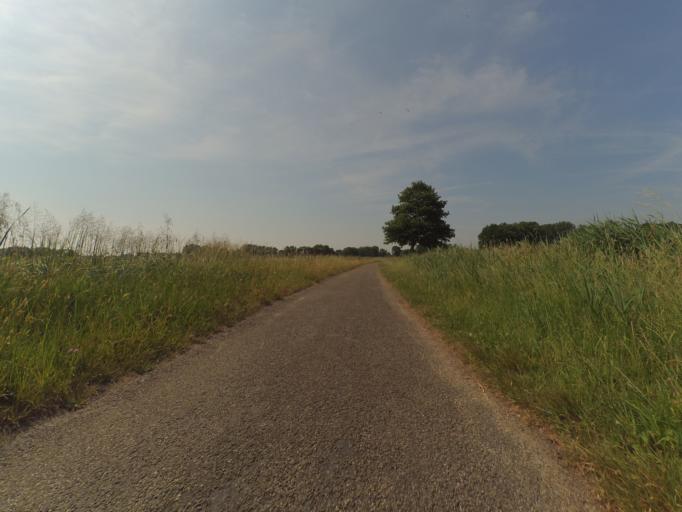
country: NL
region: North Brabant
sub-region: Gemeente Breda
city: Breda
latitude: 51.5472
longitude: 4.7880
